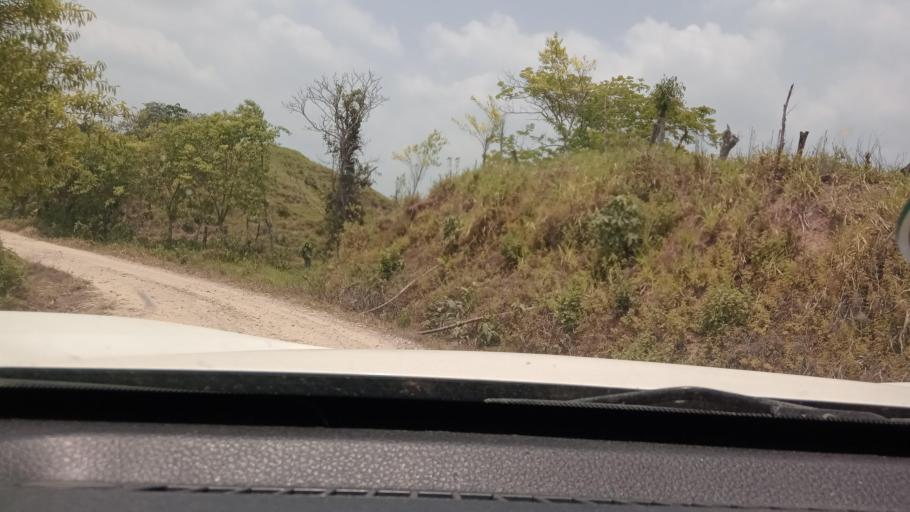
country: MX
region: Tabasco
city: Chontalpa
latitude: 17.5713
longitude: -93.7093
